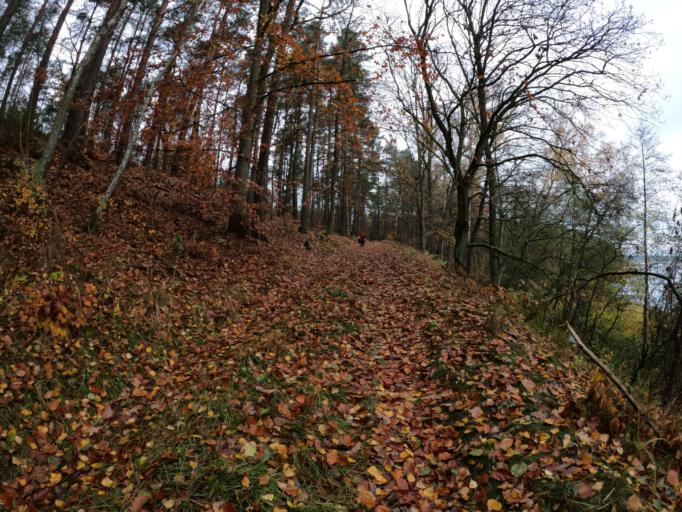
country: PL
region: West Pomeranian Voivodeship
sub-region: Powiat walecki
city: Tuczno
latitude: 53.2744
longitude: 16.2490
